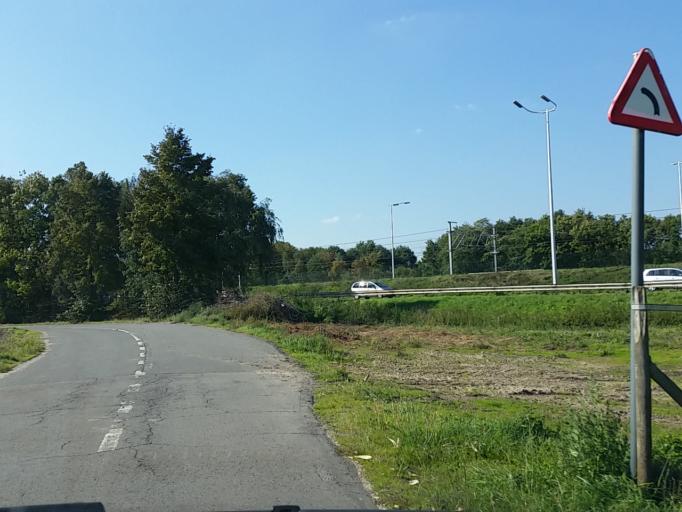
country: BE
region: Flanders
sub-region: Provincie Vlaams-Brabant
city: Machelen
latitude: 50.9296
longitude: 4.4709
